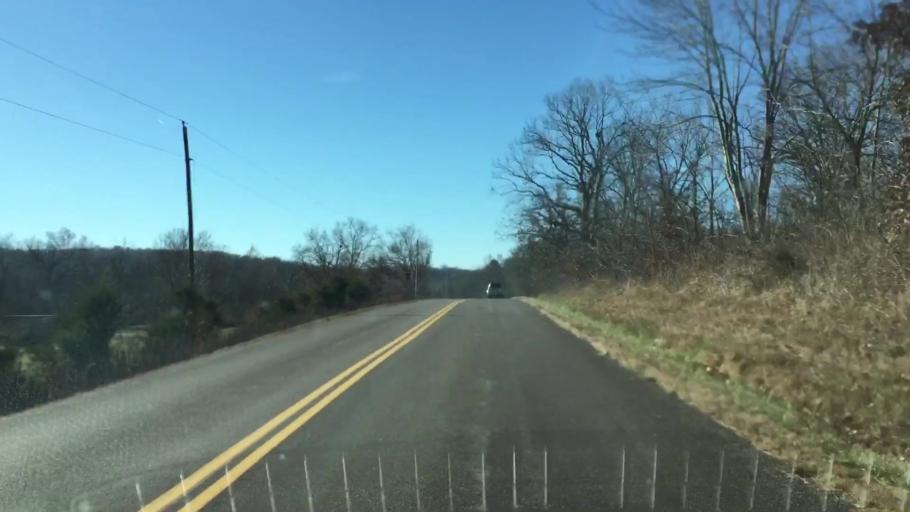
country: US
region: Missouri
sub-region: Miller County
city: Eldon
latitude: 38.3460
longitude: -92.7057
